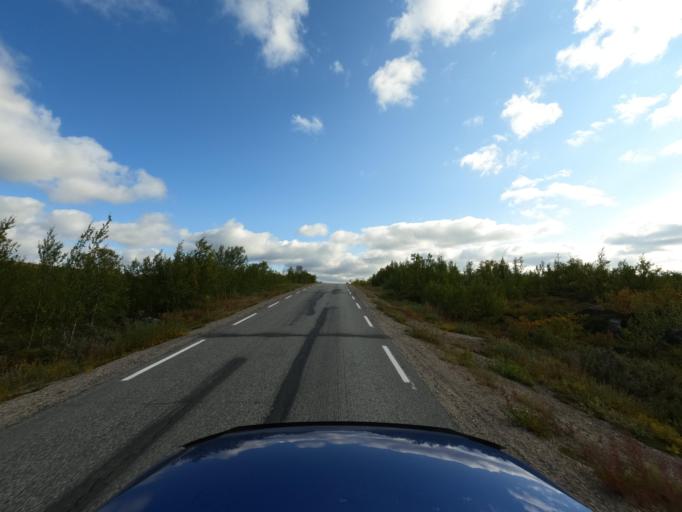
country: NO
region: Finnmark Fylke
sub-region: Porsanger
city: Lakselv
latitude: 69.3909
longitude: 24.5208
